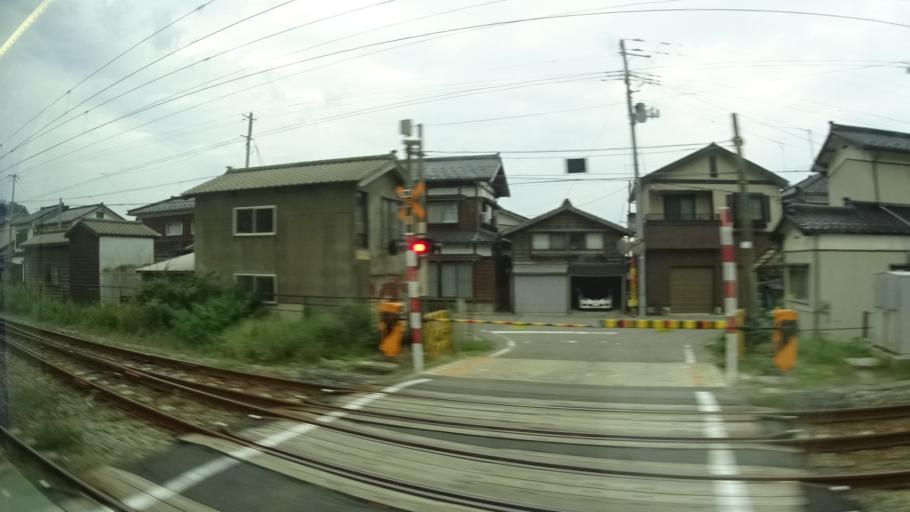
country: JP
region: Yamagata
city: Tsuruoka
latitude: 38.5526
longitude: 139.5496
